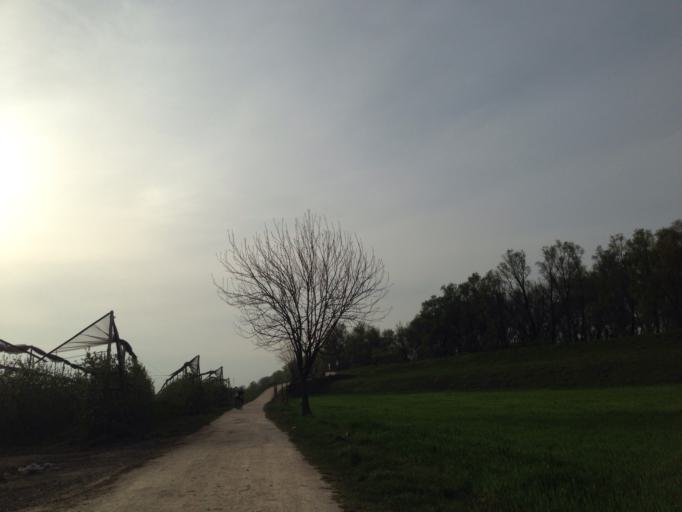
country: IT
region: Veneto
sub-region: Provincia di Verona
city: Zevio
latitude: 45.3767
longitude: 11.1195
